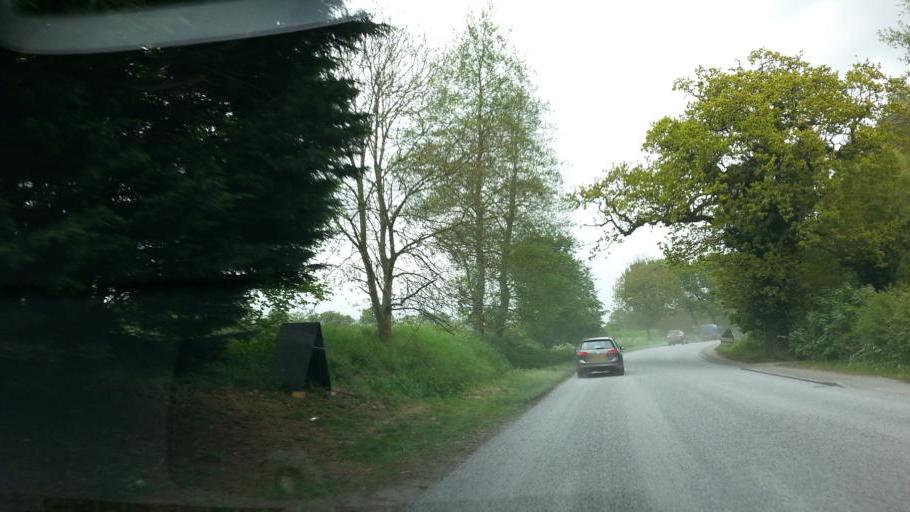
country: GB
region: England
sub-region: Suffolk
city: Bury St Edmunds
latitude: 52.2031
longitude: 0.7566
